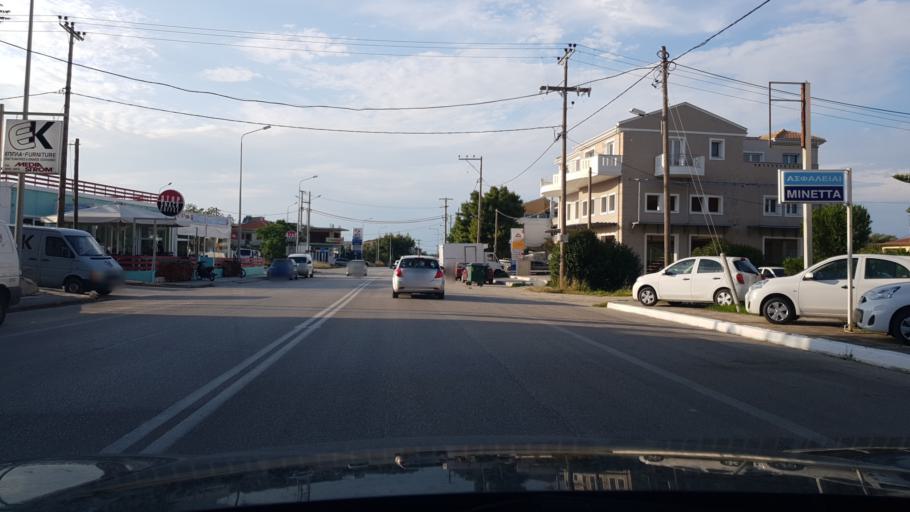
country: GR
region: Ionian Islands
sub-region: Lefkada
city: Lefkada
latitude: 38.8196
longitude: 20.7024
